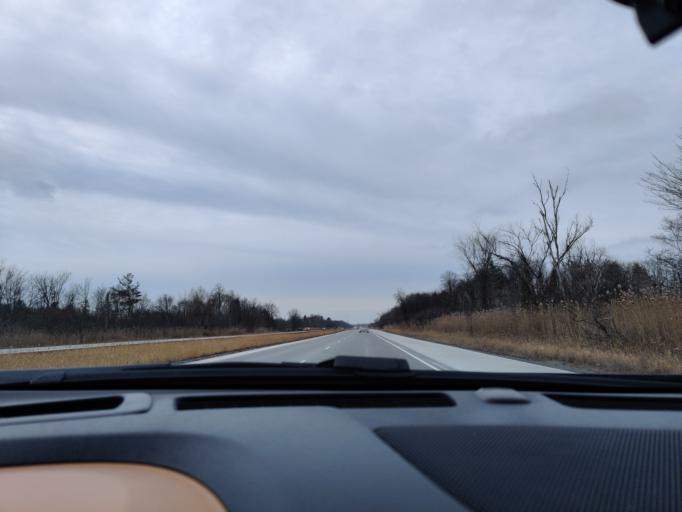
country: CA
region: Ontario
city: Cornwall
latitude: 45.0804
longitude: -74.6177
